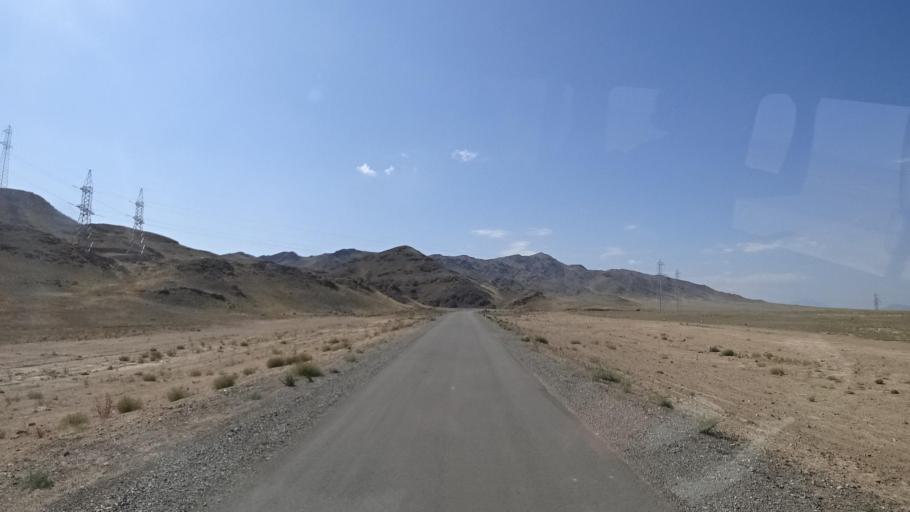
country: KZ
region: Almaty Oblysy
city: Kegen
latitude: 43.3480
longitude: 78.9322
